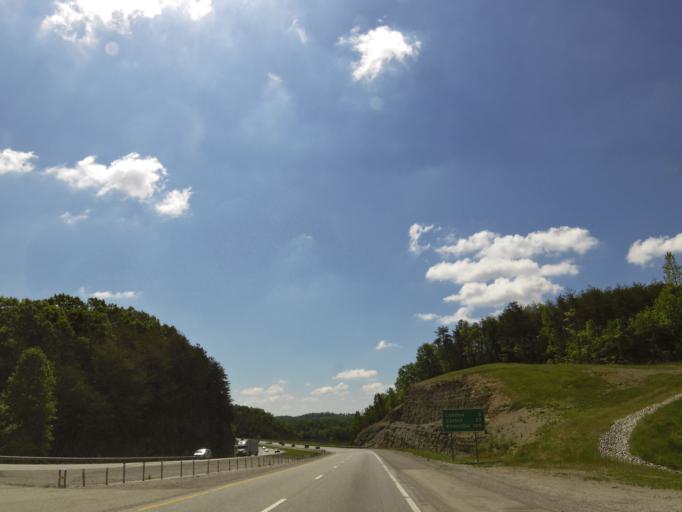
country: US
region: Kentucky
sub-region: Laurel County
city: London
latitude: 37.2168
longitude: -84.2017
